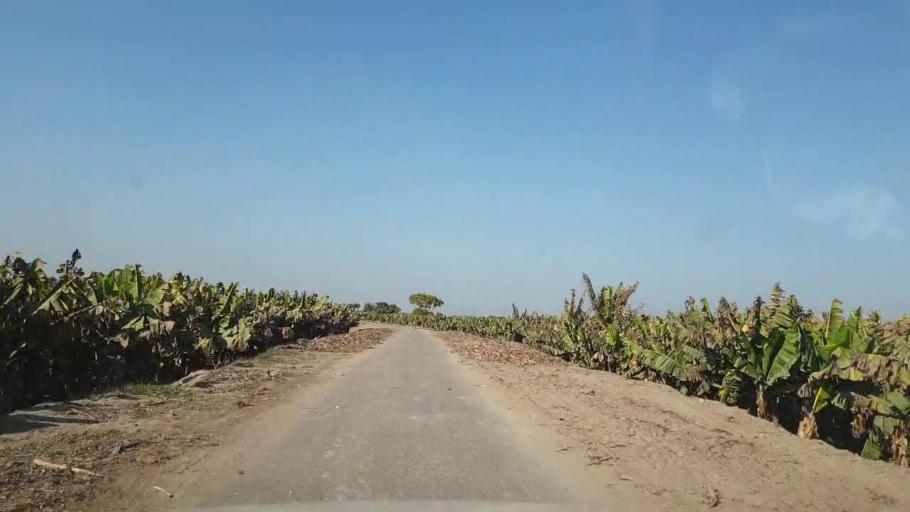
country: PK
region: Sindh
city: Tando Allahyar
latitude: 25.4755
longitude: 68.6606
